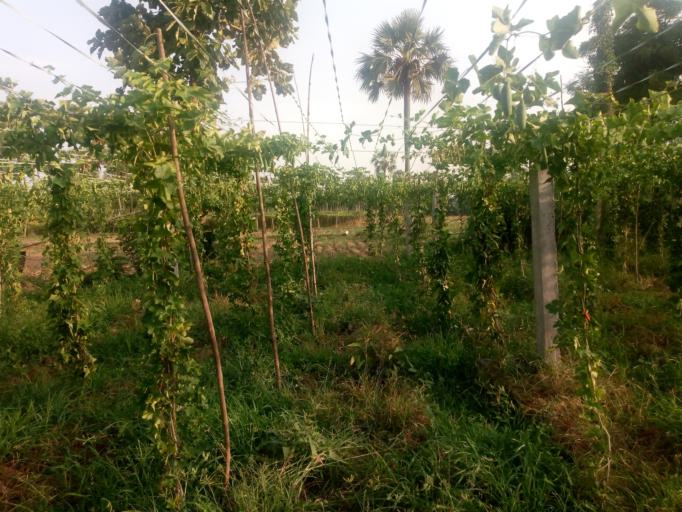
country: IN
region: Andhra Pradesh
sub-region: West Godavari
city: Tadepallegudem
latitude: 16.8576
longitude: 81.3195
